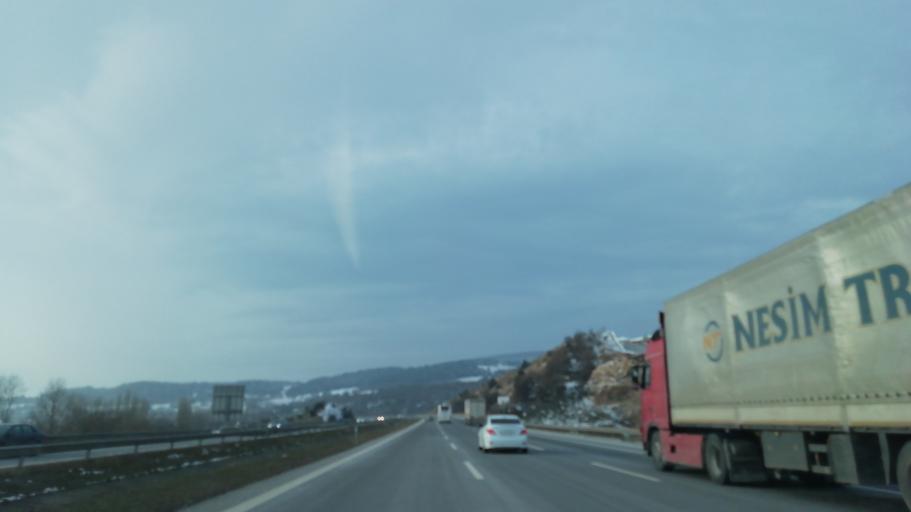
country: TR
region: Bolu
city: Bolu
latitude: 40.7394
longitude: 31.5493
